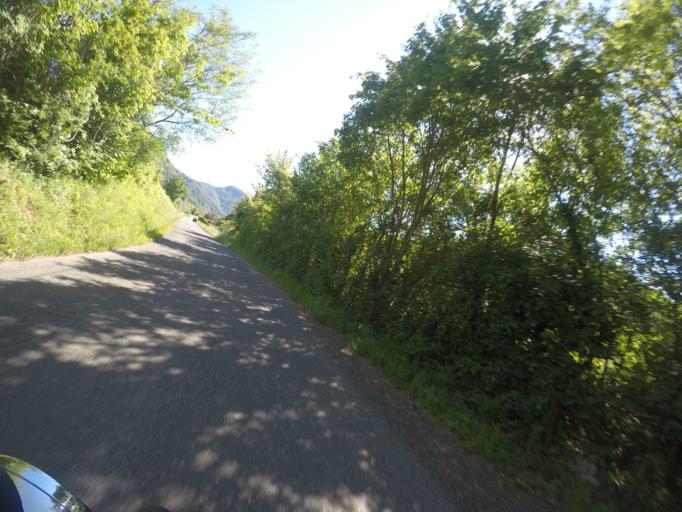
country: IT
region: Tuscany
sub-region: Provincia di Massa-Carrara
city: Fosdinovo
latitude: 44.1478
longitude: 10.1000
